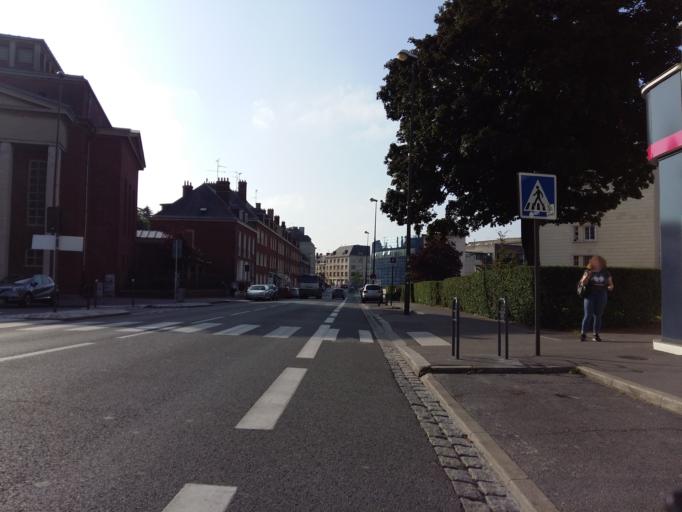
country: FR
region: Picardie
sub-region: Departement de la Somme
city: Amiens
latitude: 49.8954
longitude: 2.2907
